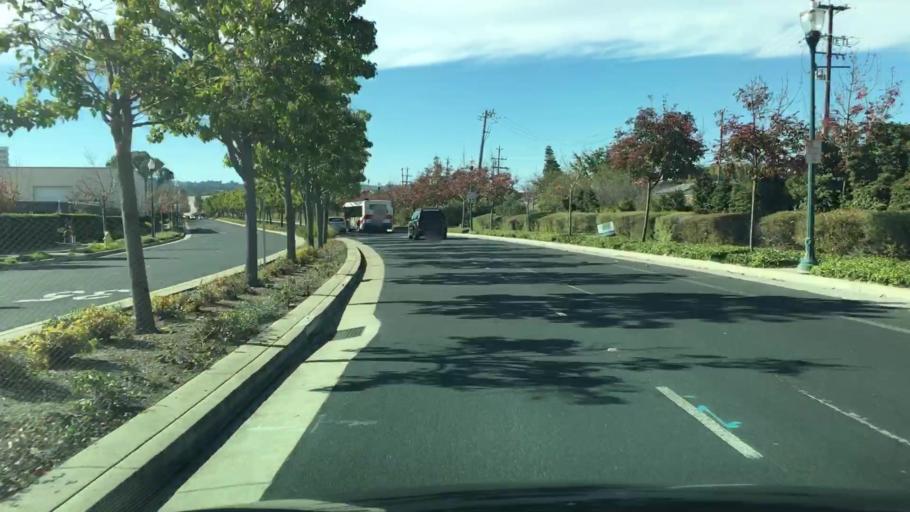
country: US
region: California
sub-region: San Mateo County
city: San Mateo
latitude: 37.5485
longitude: -122.3000
